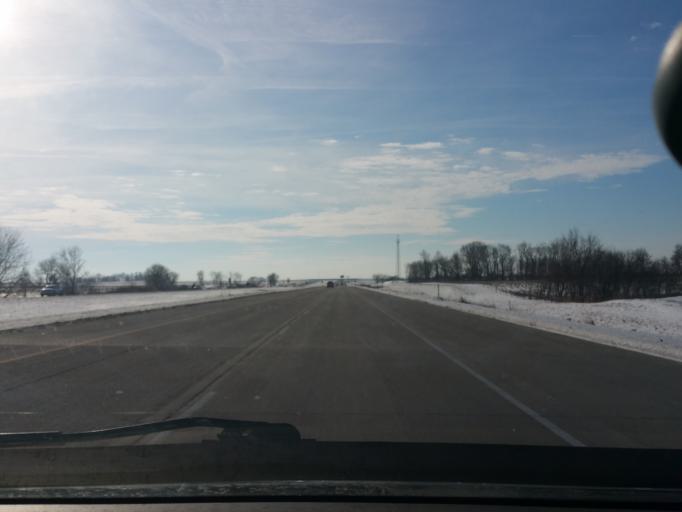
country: US
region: Iowa
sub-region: Warren County
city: Norwalk
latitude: 41.4976
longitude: -93.7806
